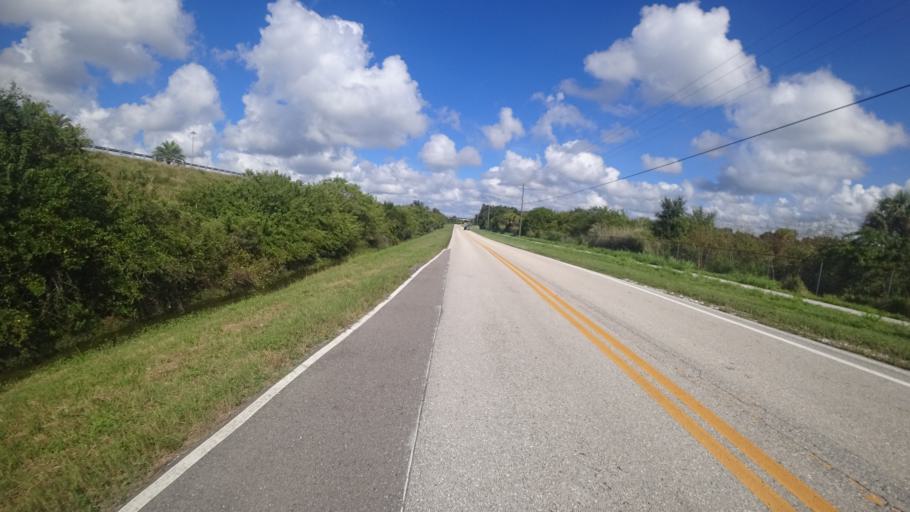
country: US
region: Florida
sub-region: Manatee County
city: Ellenton
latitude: 27.5808
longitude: -82.5133
